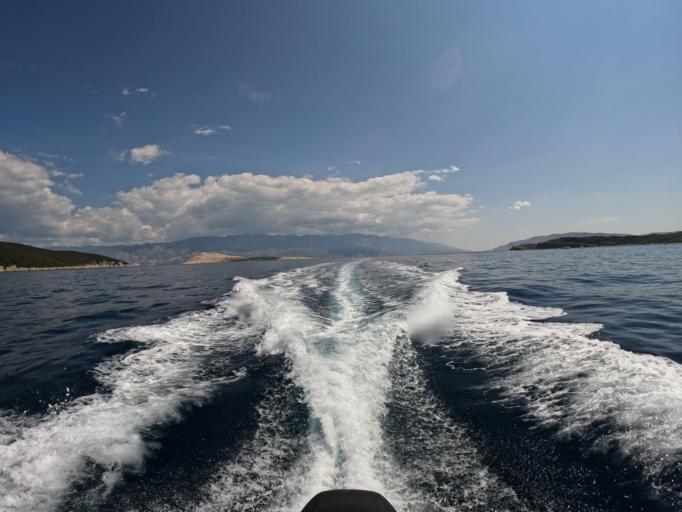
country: HR
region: Primorsko-Goranska
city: Lopar
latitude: 44.8531
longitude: 14.7543
